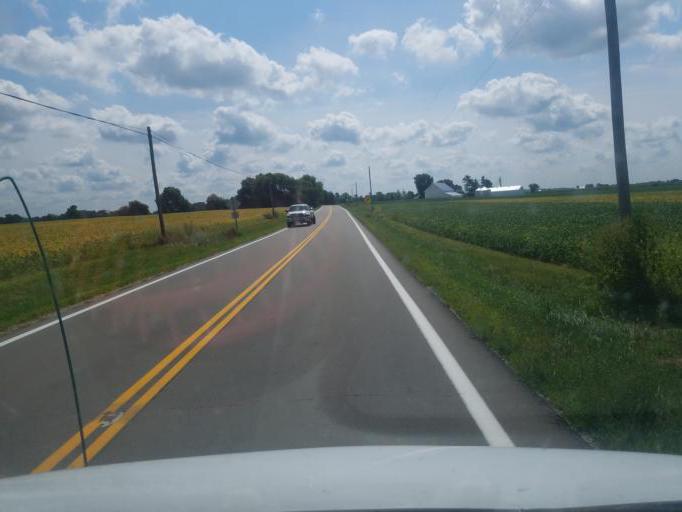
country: US
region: Ohio
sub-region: Marion County
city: Prospect
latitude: 40.4035
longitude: -83.1647
